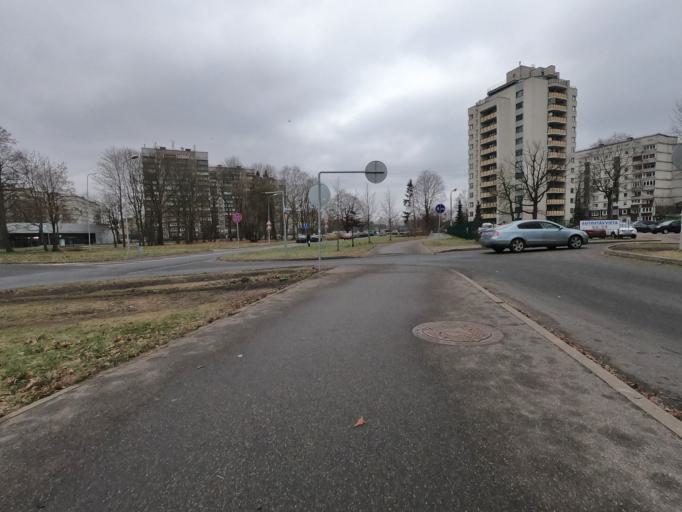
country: LV
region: Marupe
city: Marupe
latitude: 56.9456
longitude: 24.0135
